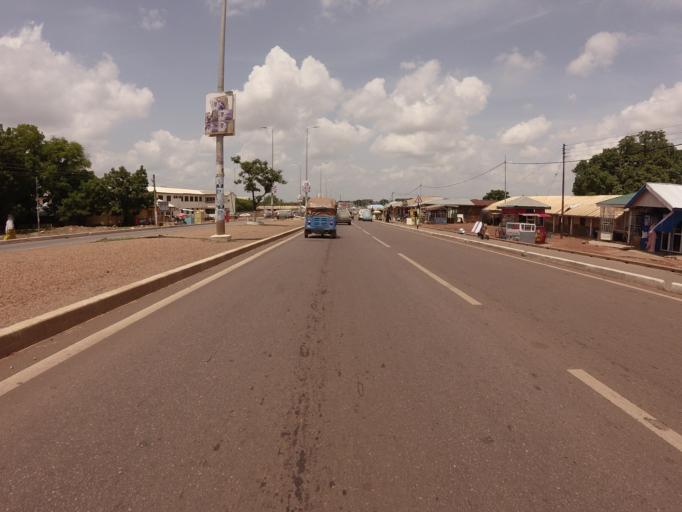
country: GH
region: Northern
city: Tamale
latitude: 9.3996
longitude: -0.8328
